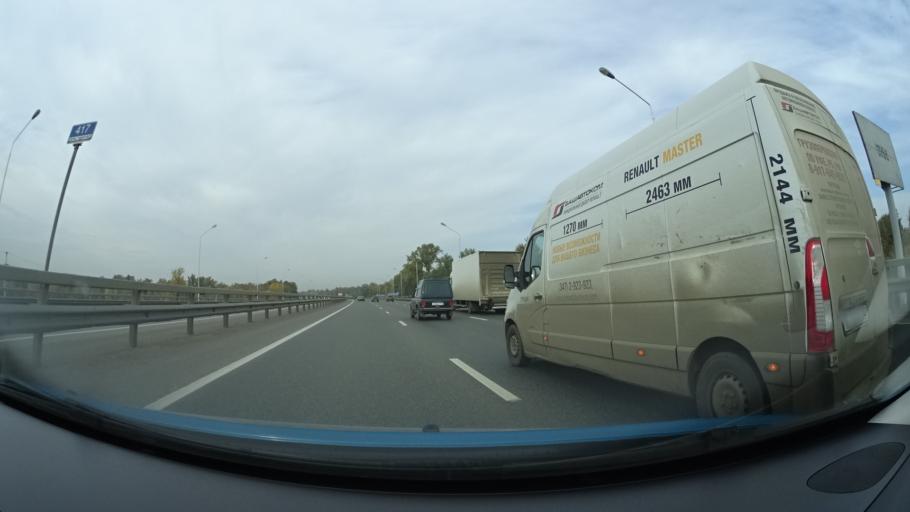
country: RU
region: Bashkortostan
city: Ufa
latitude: 54.6563
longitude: 55.8942
